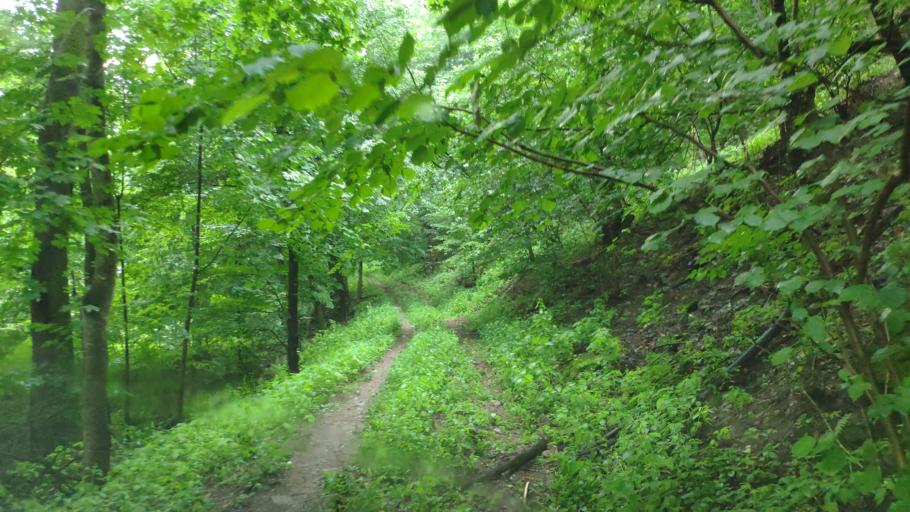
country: SK
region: Presovsky
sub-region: Okres Presov
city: Presov
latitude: 48.8667
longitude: 21.2074
